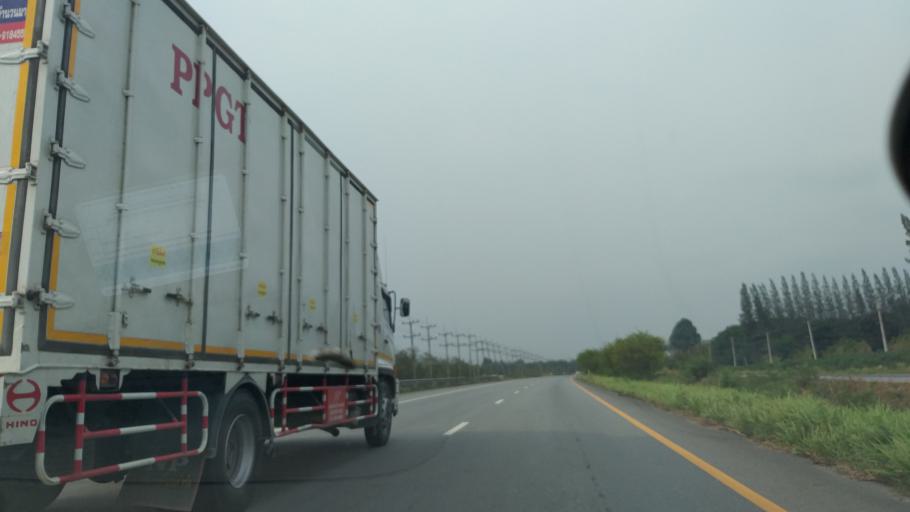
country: TH
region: Chon Buri
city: Ban Bueng
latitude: 13.2589
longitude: 101.2474
